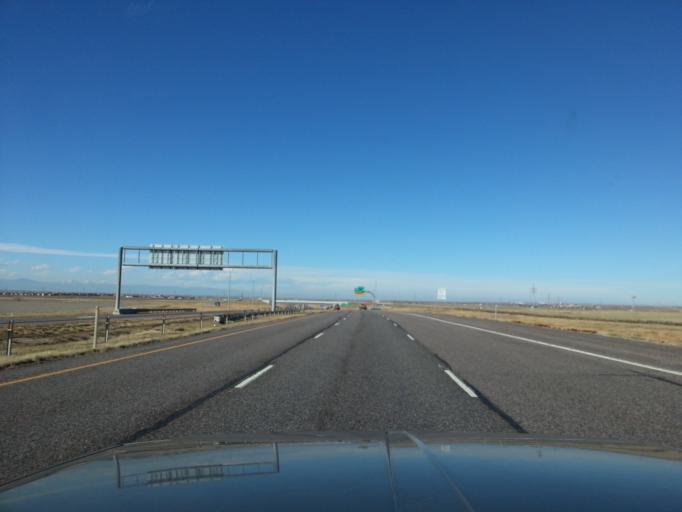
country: US
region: Colorado
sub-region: Adams County
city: Brighton
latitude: 39.8657
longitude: -104.7522
